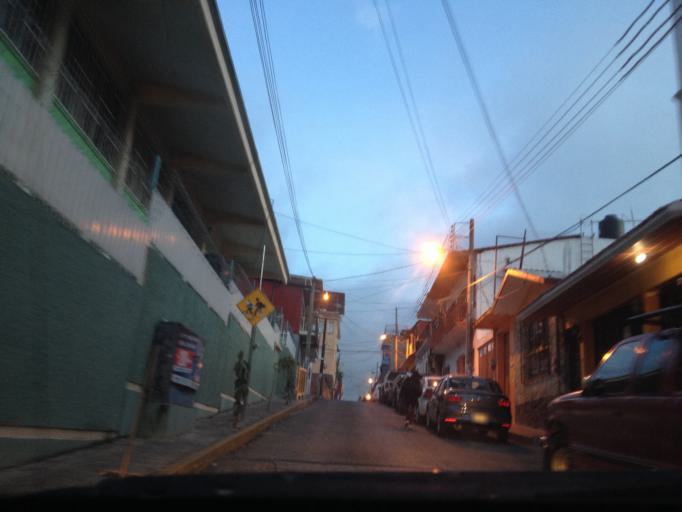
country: MX
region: Guerrero
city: Chilpancingo de los Bravos
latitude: 17.5563
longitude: -99.4992
